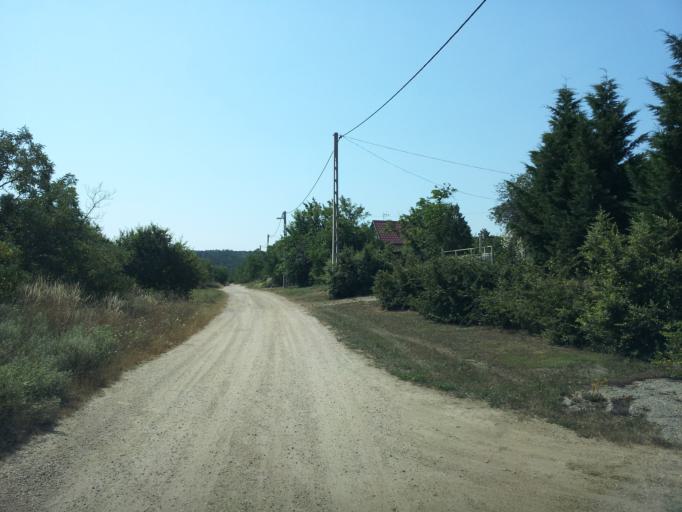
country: HU
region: Fejer
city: Pakozd
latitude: 47.2597
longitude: 18.5099
